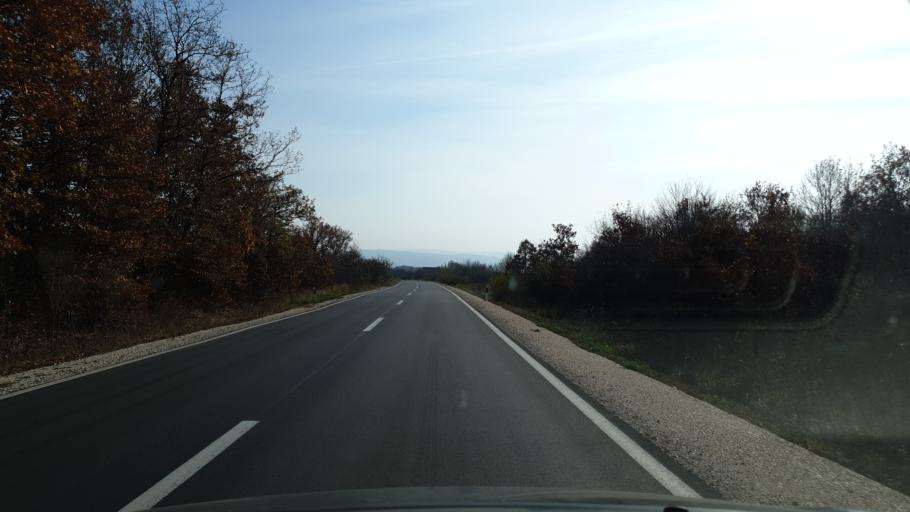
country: RS
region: Central Serbia
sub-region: Borski Okrug
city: Bor
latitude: 43.9810
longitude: 22.0726
